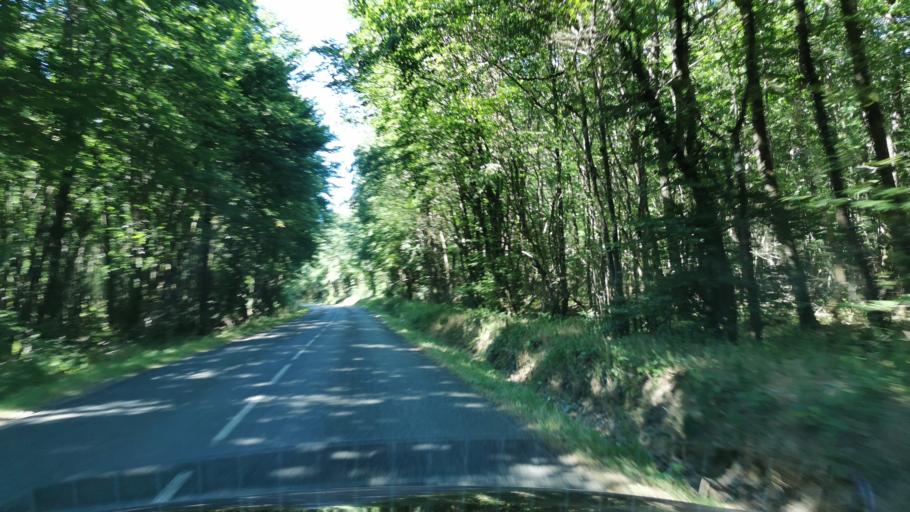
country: FR
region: Bourgogne
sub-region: Departement de Saone-et-Loire
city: Torcy
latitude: 46.7750
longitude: 4.4726
